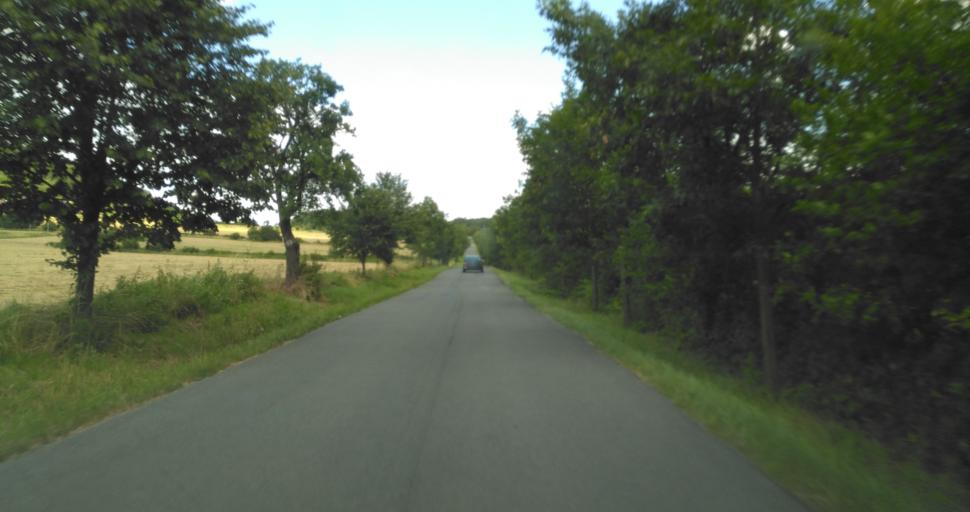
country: CZ
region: Central Bohemia
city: Zebrak
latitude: 49.9364
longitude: 13.8792
